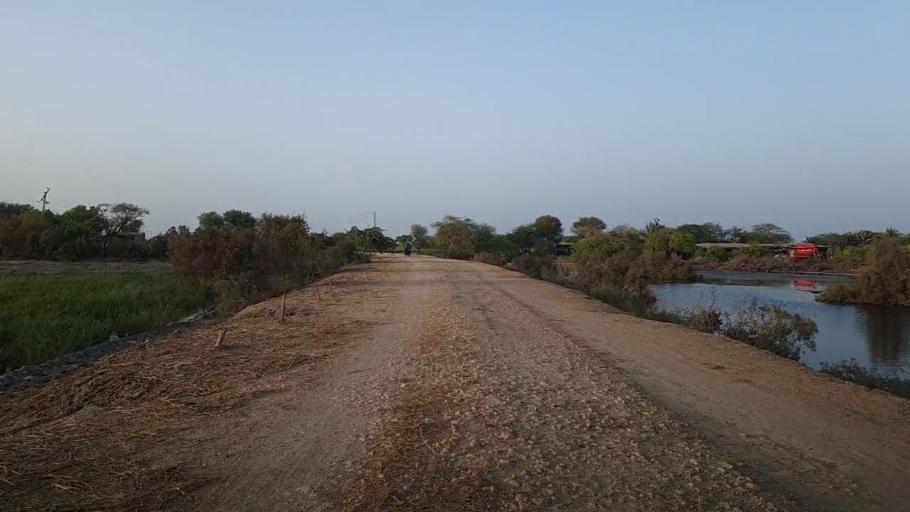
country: PK
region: Sindh
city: Kario
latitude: 24.7202
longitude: 68.4629
